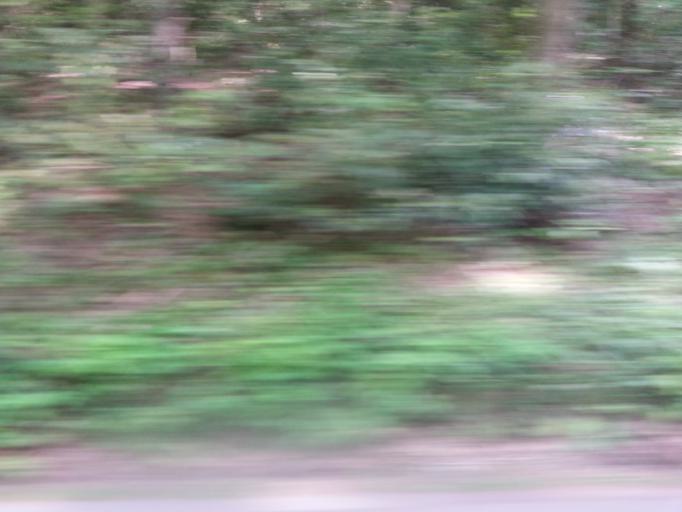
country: US
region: Tennessee
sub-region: Sevier County
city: Gatlinburg
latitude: 35.6746
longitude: -83.6622
